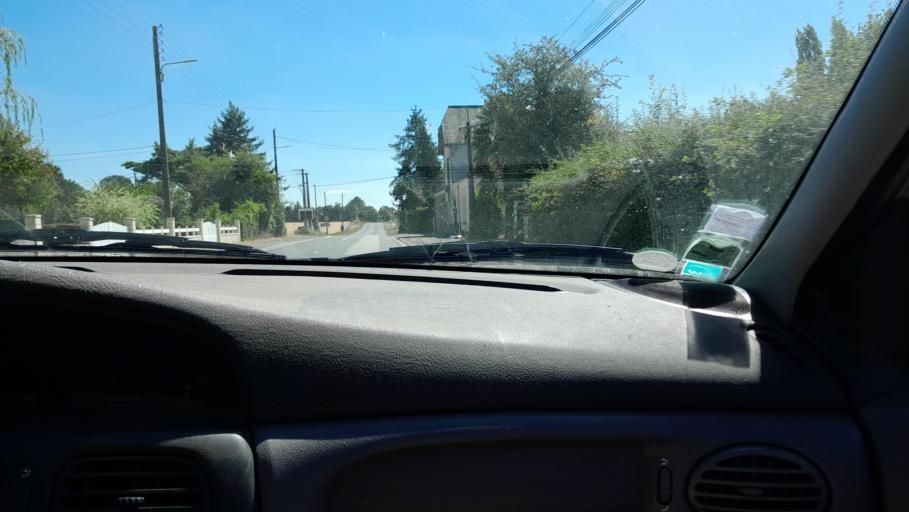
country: FR
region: Pays de la Loire
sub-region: Departement de la Loire-Atlantique
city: Saint-Mars-la-Jaille
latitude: 47.6193
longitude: -1.1984
